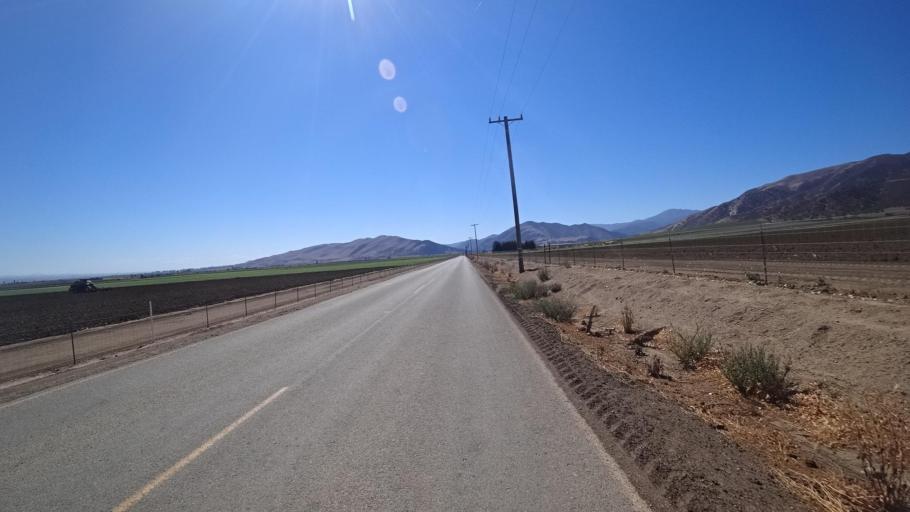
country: US
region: California
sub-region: Monterey County
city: Greenfield
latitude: 36.3210
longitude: -121.3165
